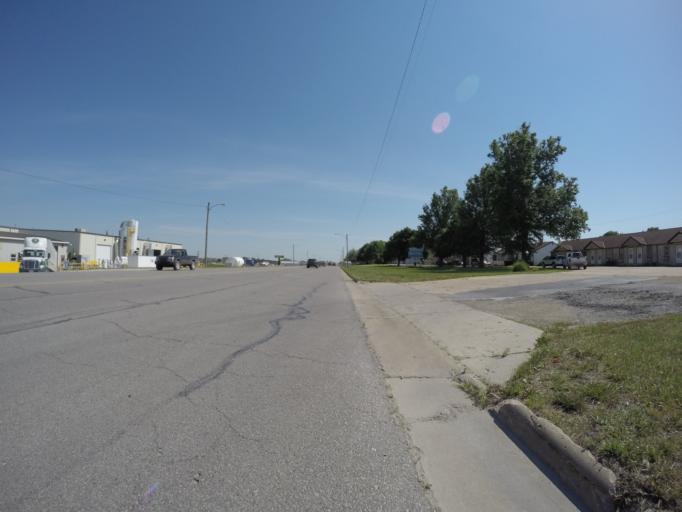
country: US
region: Kansas
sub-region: Nemaha County
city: Sabetha
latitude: 39.8973
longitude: -95.7884
